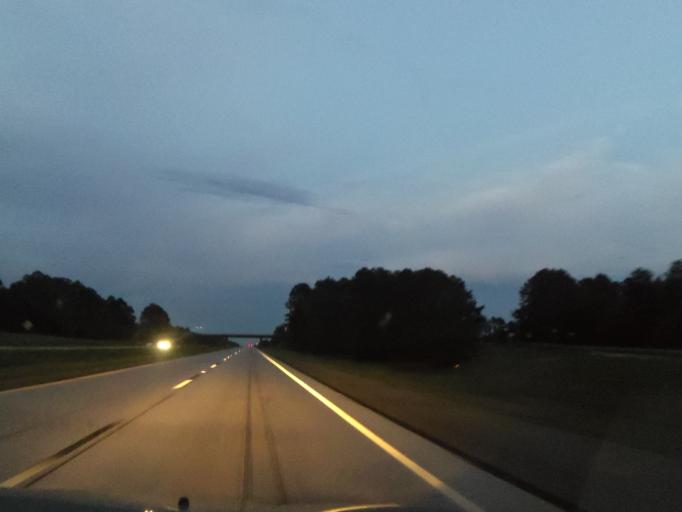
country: US
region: Georgia
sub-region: McDuffie County
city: Thomson
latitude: 33.5114
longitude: -82.4491
